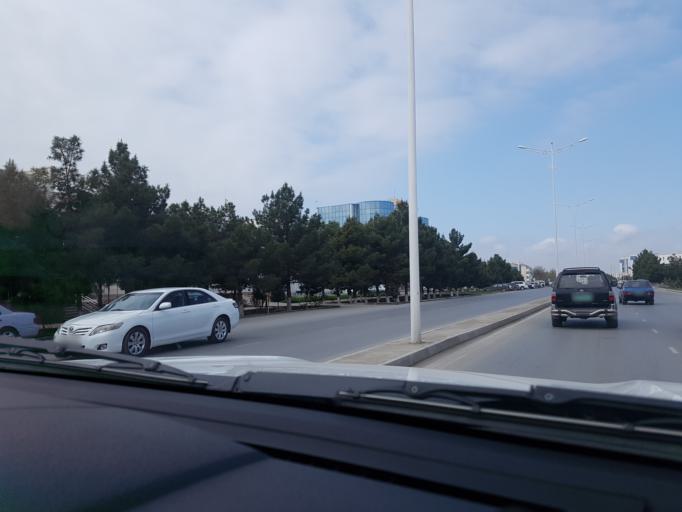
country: TM
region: Lebap
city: Turkmenabat
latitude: 39.0724
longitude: 63.5896
